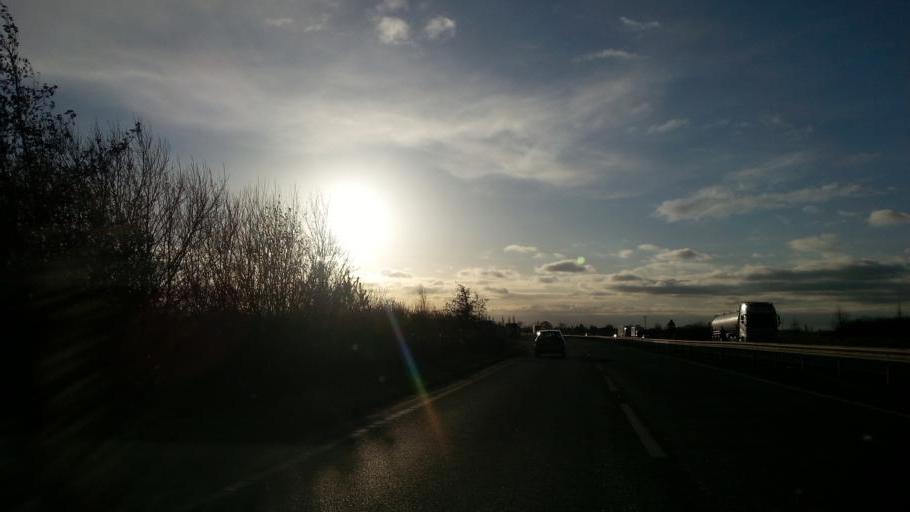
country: GB
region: England
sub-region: Peterborough
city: Thorney
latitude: 52.6251
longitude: -0.1135
